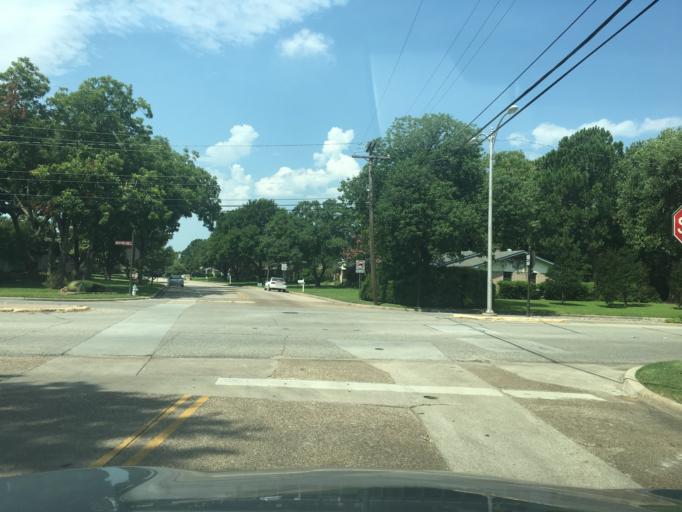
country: US
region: Texas
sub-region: Dallas County
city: Farmers Branch
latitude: 32.9340
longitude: -96.8659
